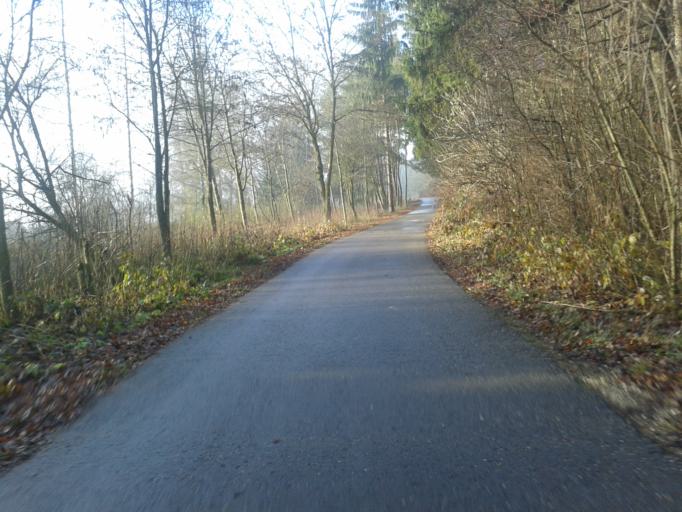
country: DE
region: Baden-Wuerttemberg
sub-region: Tuebingen Region
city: Erbach
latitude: 48.3747
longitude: 9.8786
